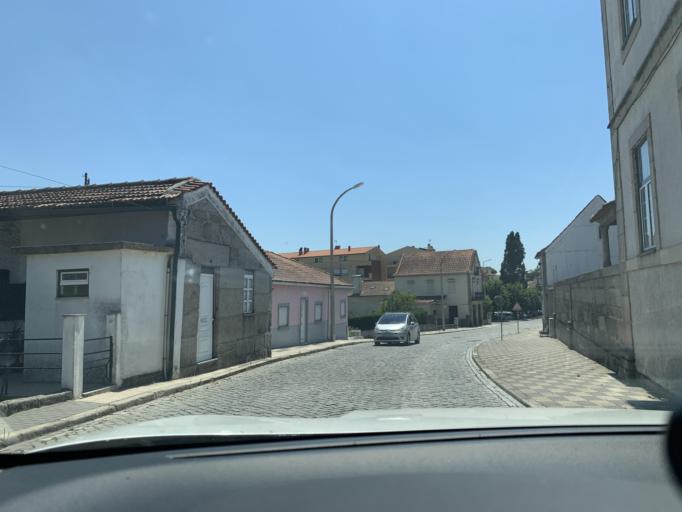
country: PT
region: Viseu
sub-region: Nelas
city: Nelas
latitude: 40.5338
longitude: -7.8486
